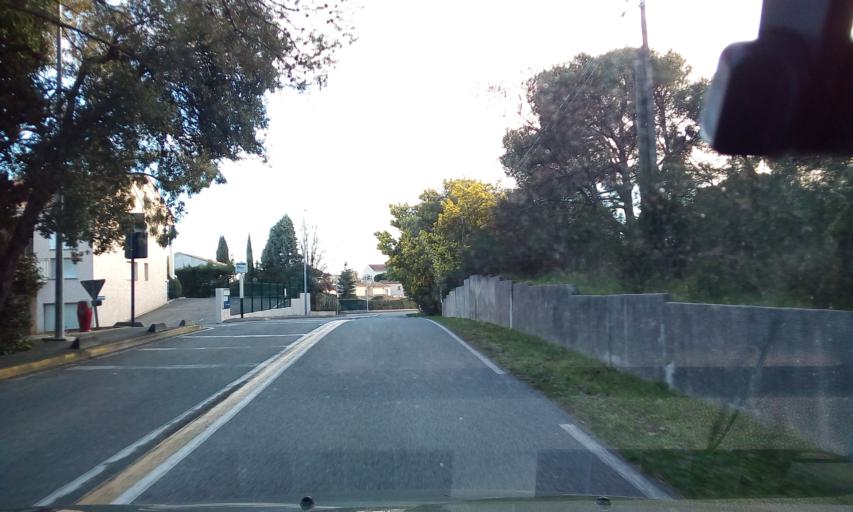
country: FR
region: Provence-Alpes-Cote d'Azur
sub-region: Departement du Var
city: Saint-Raphael
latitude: 43.4388
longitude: 6.7669
